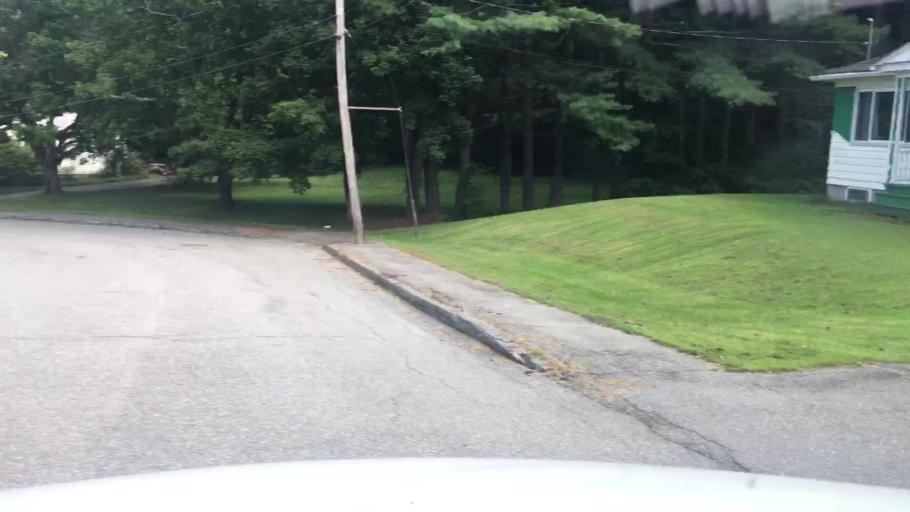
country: US
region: Maine
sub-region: Kennebec County
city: Augusta
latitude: 44.3186
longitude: -69.7786
